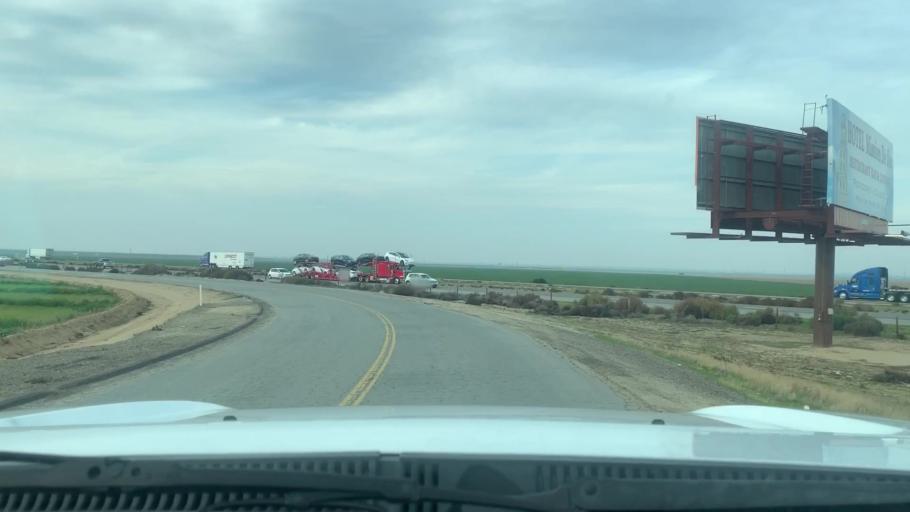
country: US
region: California
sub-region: Kern County
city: Buttonwillow
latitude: 35.4428
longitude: -119.4588
